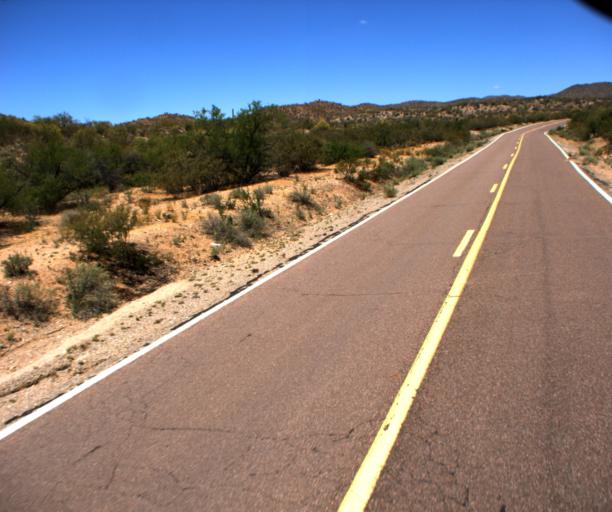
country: US
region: Arizona
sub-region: Yavapai County
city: Bagdad
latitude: 34.4462
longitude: -113.2426
